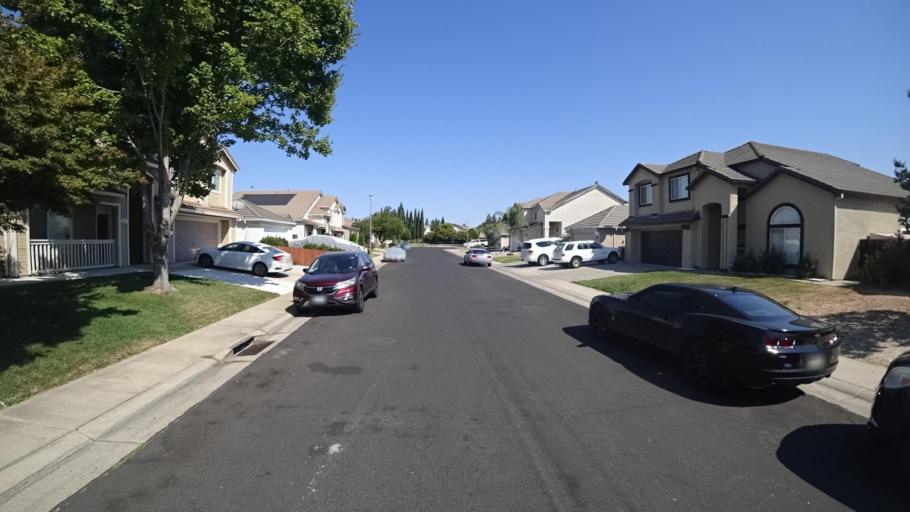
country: US
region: California
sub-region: Sacramento County
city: Vineyard
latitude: 38.4498
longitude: -121.3865
